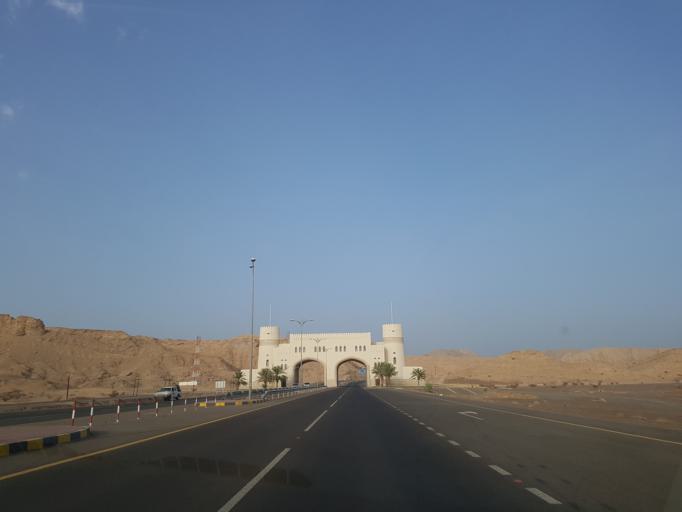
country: OM
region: Al Buraimi
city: Al Buraymi
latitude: 24.2328
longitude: 55.9338
